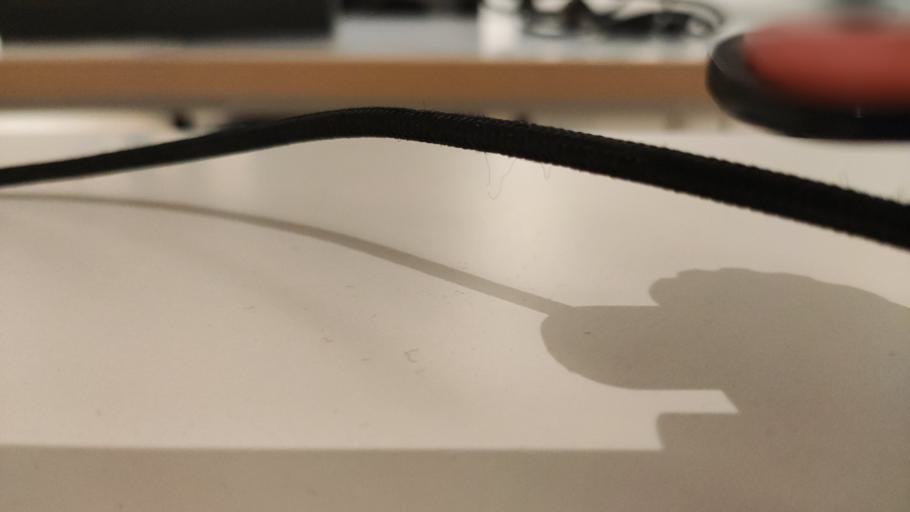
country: RU
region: Moskovskaya
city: Dorokhovo
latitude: 55.5295
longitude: 36.3580
